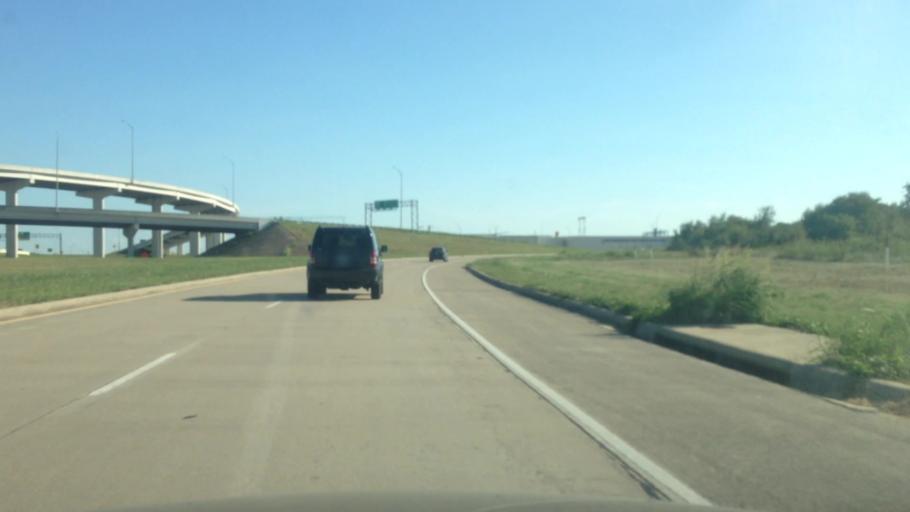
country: US
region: Texas
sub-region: Tarrant County
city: Euless
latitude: 32.8407
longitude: -97.0621
